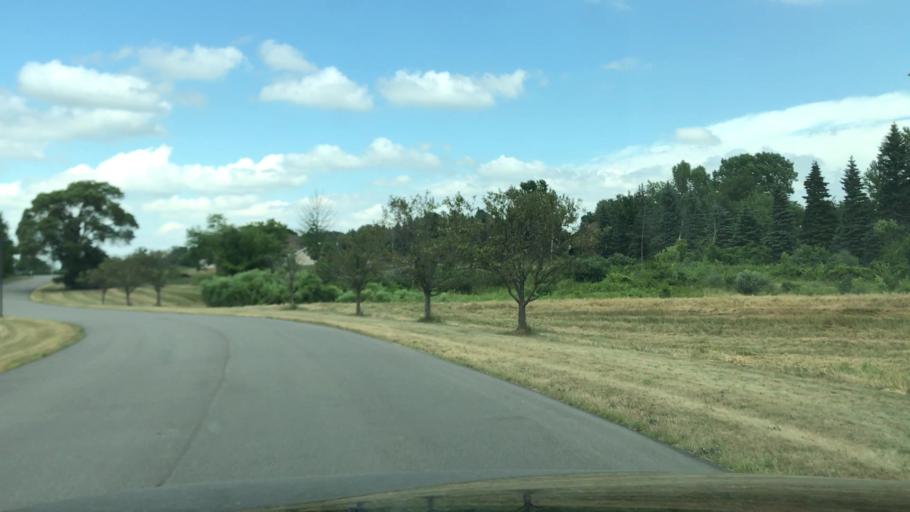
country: US
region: Michigan
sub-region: Ottawa County
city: Holland
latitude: 42.7734
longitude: -86.0684
